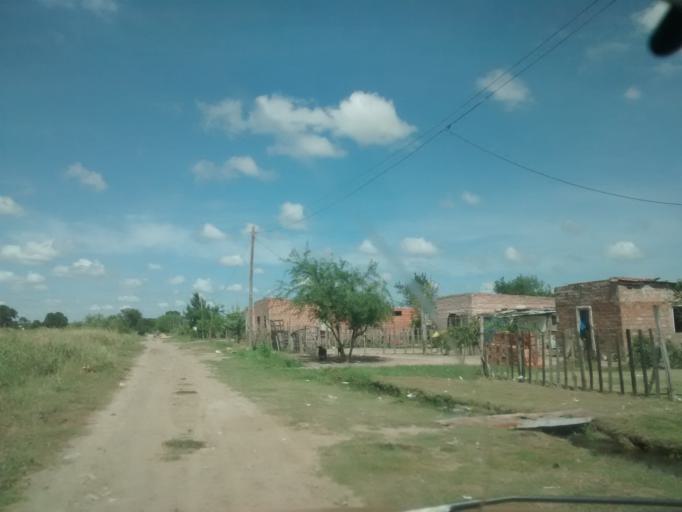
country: AR
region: Chaco
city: Fontana
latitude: -27.4651
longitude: -59.0313
